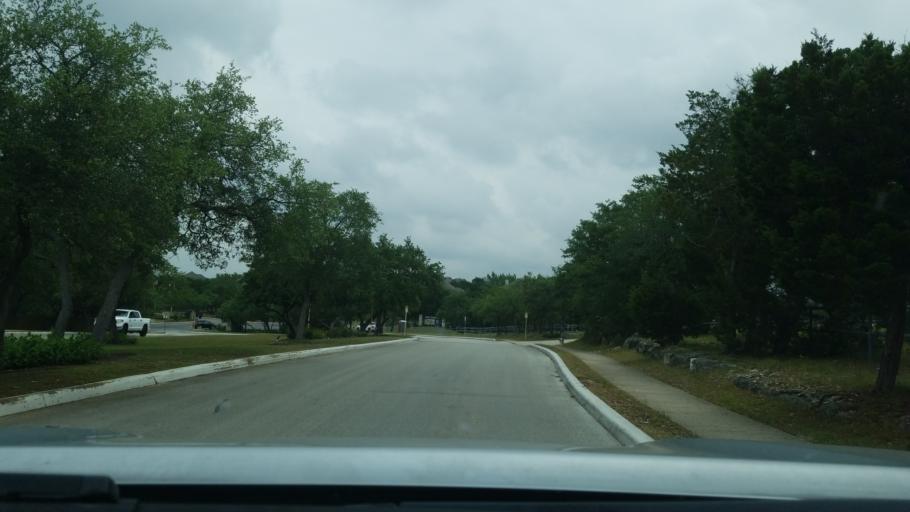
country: US
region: Texas
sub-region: Bexar County
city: Timberwood Park
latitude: 29.6843
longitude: -98.4615
